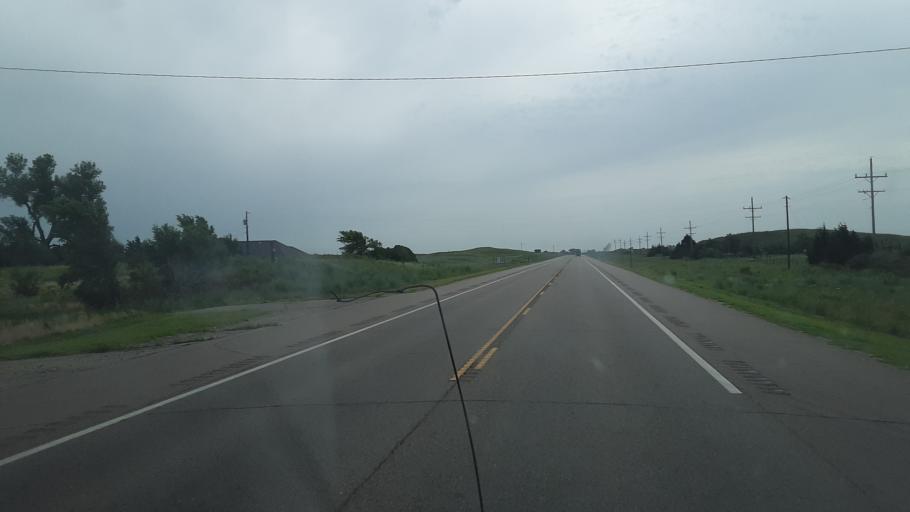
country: US
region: Kansas
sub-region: Edwards County
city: Kinsley
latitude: 37.9279
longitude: -99.3669
